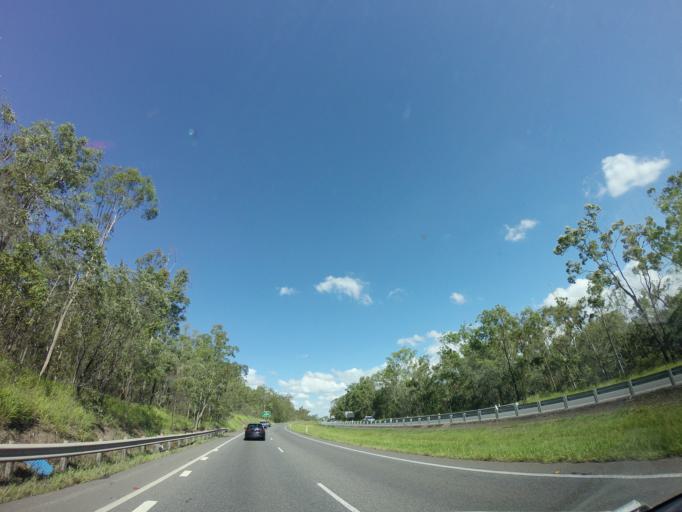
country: AU
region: Queensland
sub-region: Ipswich
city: North Booval
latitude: -27.5737
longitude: 152.7952
